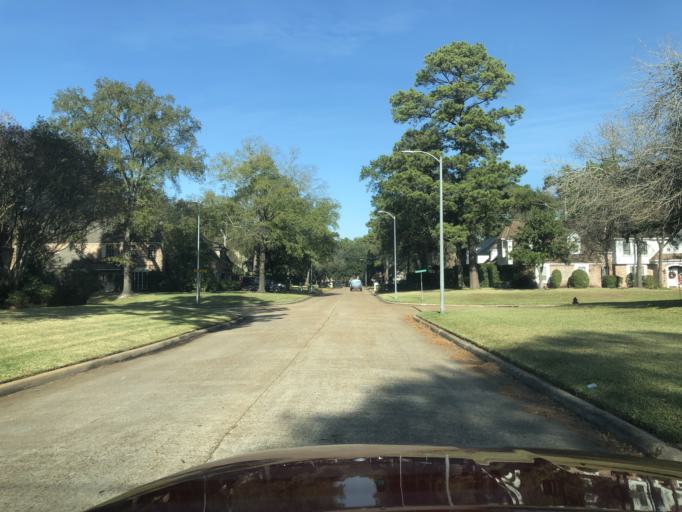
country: US
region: Texas
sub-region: Harris County
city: Spring
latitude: 30.0148
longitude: -95.4628
